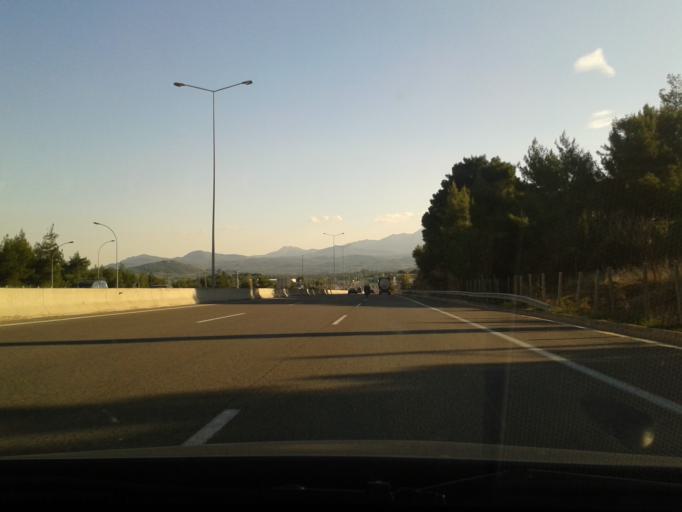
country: GR
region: Attica
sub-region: Nomarchia Anatolikis Attikis
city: Polydendri
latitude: 38.2229
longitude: 23.8513
